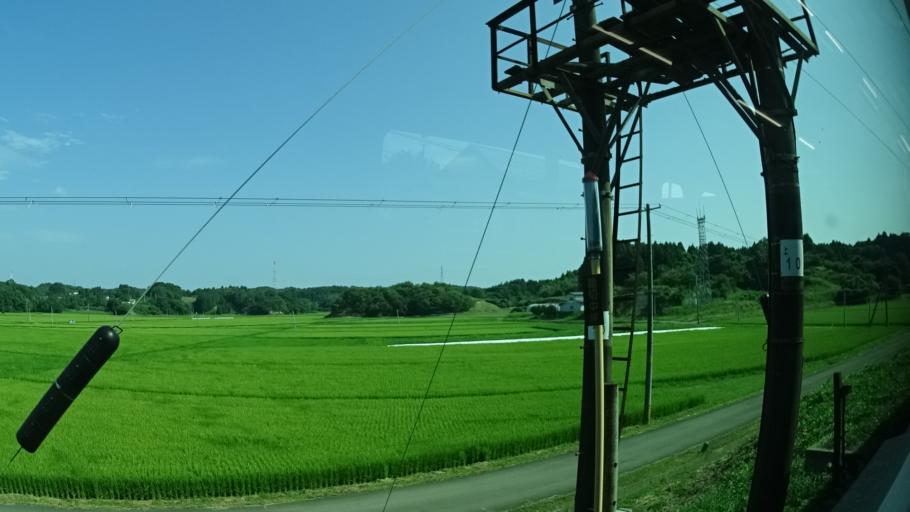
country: JP
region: Miyagi
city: Matsushima
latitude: 38.4317
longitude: 141.0828
